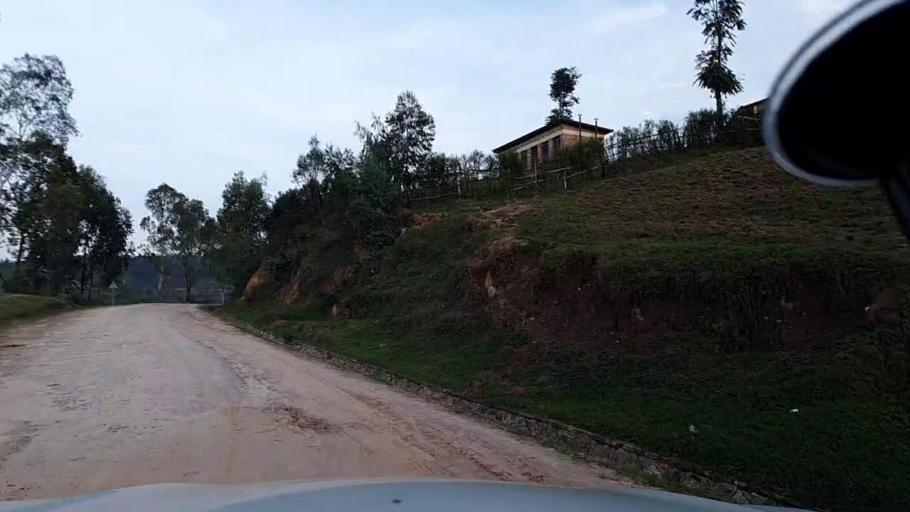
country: RW
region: Southern Province
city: Nyanza
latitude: -2.2231
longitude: 29.6489
